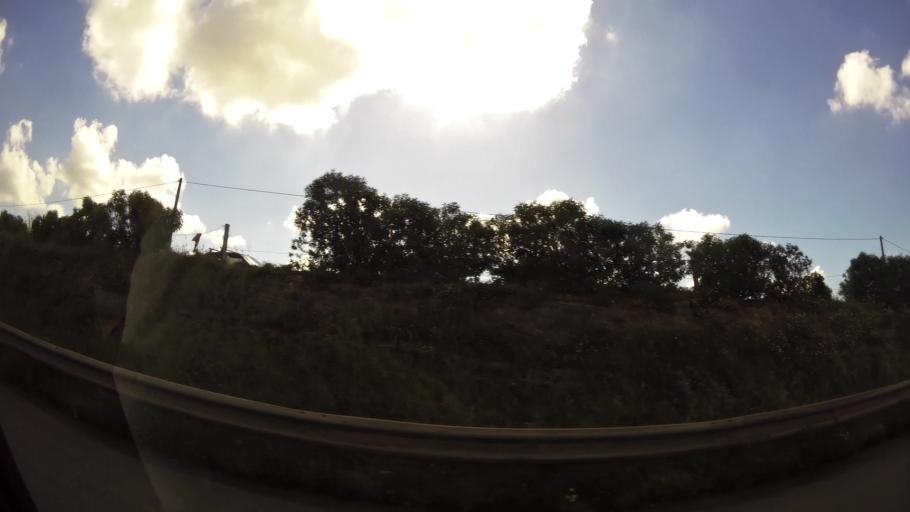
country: MA
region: Grand Casablanca
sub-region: Nouaceur
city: Bouskoura
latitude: 33.4435
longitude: -7.6316
